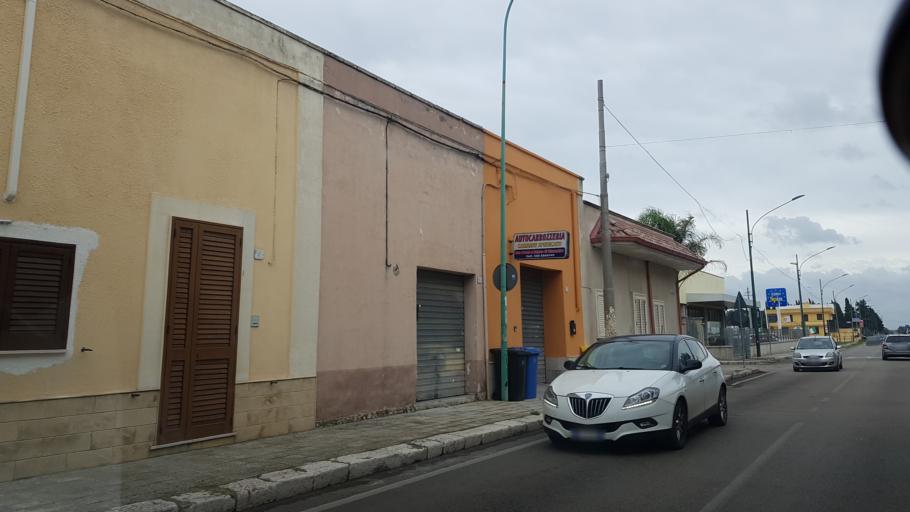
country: IT
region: Apulia
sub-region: Provincia di Lecce
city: Guagnano
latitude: 40.4013
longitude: 17.9544
